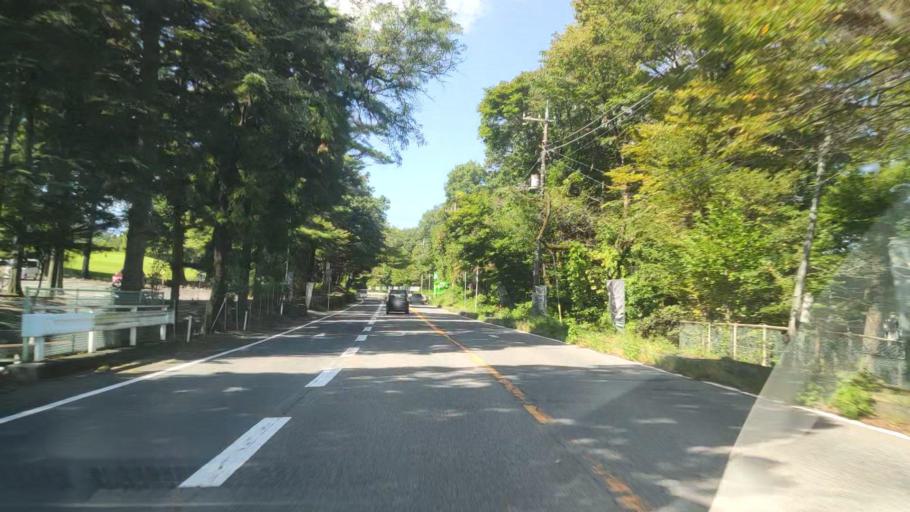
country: JP
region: Gunma
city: Shibukawa
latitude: 36.4987
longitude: 138.9390
